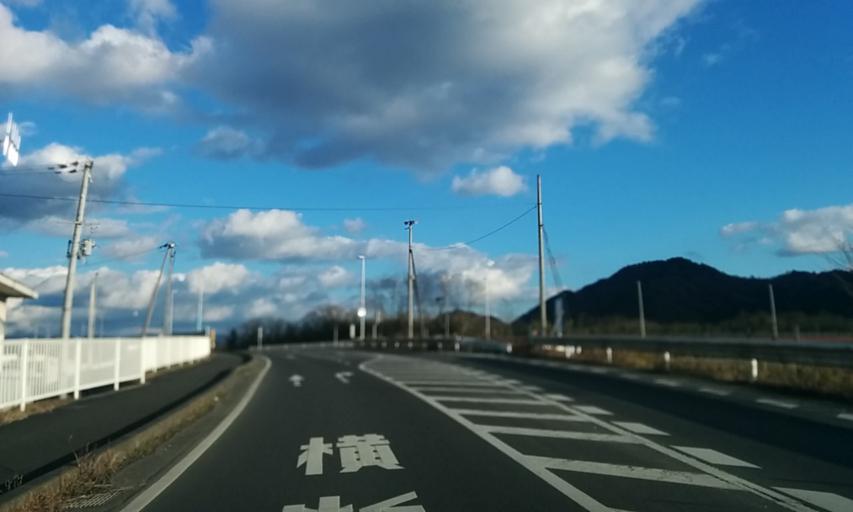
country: JP
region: Kyoto
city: Ayabe
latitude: 35.3102
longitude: 135.2035
